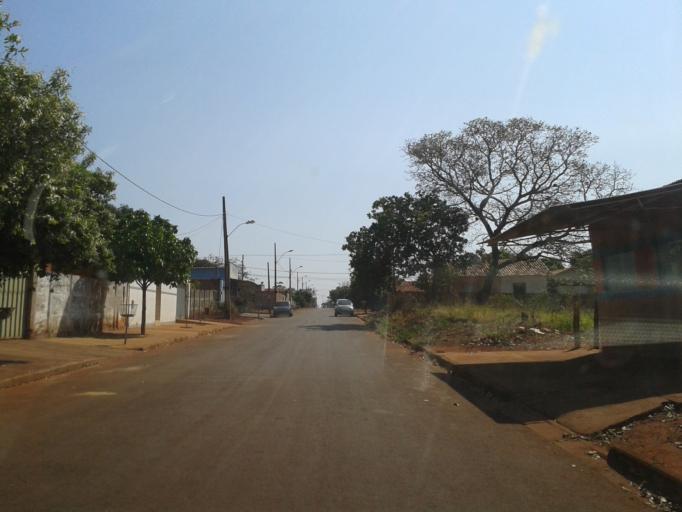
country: BR
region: Minas Gerais
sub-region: Ituiutaba
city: Ituiutaba
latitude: -18.9607
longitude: -49.4837
